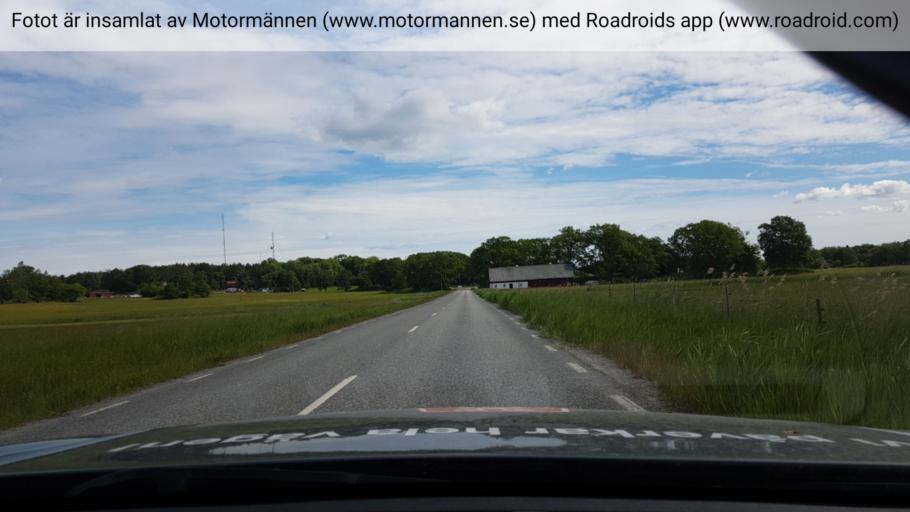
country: SE
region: Stockholm
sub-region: Haninge Kommun
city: Jordbro
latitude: 59.0030
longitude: 18.1147
